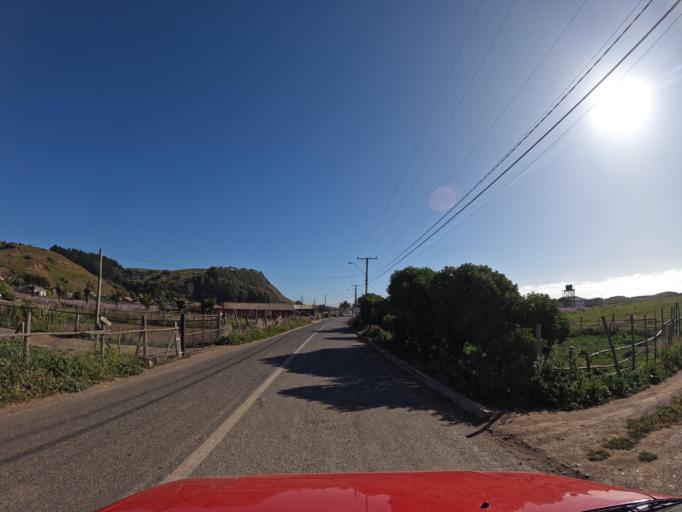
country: CL
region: Maule
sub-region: Provincia de Talca
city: Constitucion
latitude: -34.8540
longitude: -72.1427
